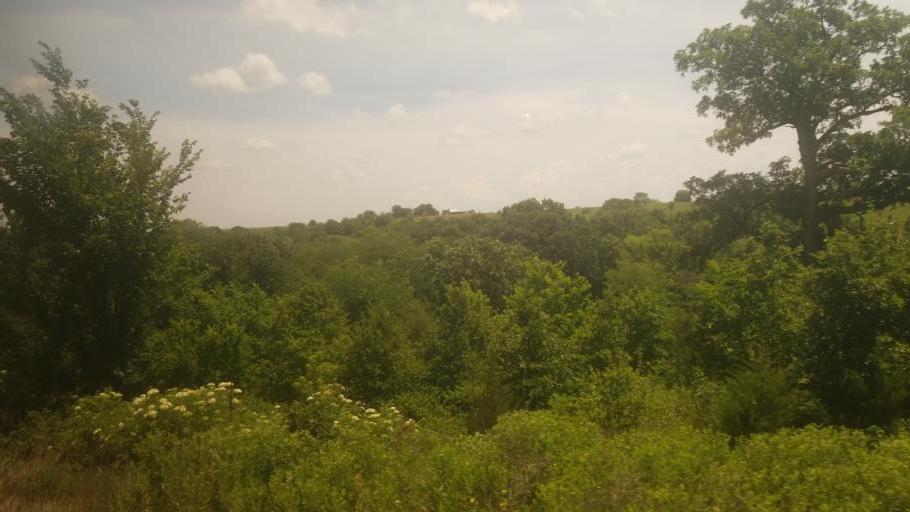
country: US
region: Missouri
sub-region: Linn County
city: Marceline
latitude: 39.8460
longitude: -92.8162
